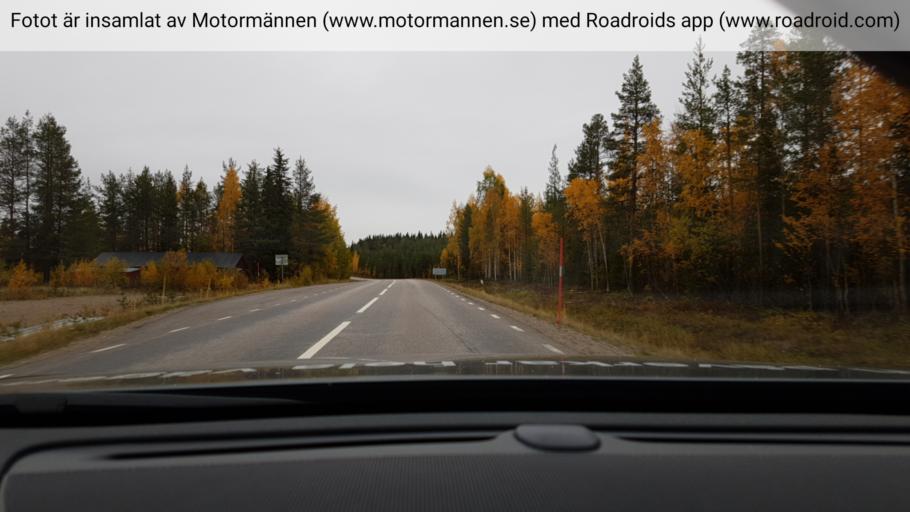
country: SE
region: Norrbotten
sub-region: Overkalix Kommun
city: OEverkalix
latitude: 66.5507
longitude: 22.7581
